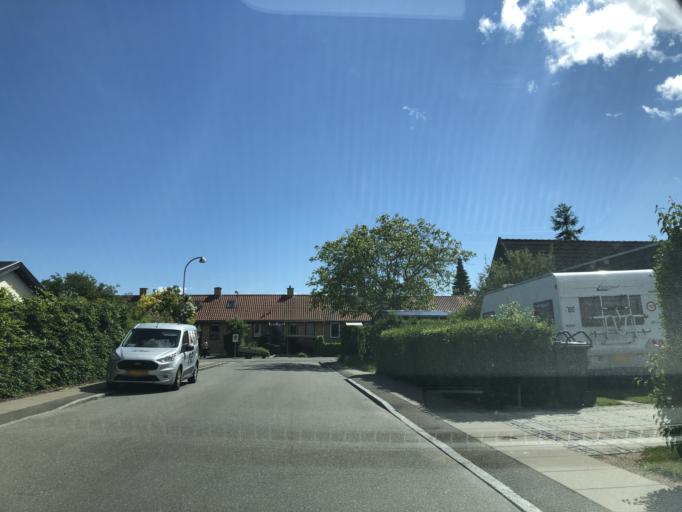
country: DK
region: Capital Region
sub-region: Hvidovre Kommune
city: Hvidovre
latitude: 55.6607
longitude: 12.4670
